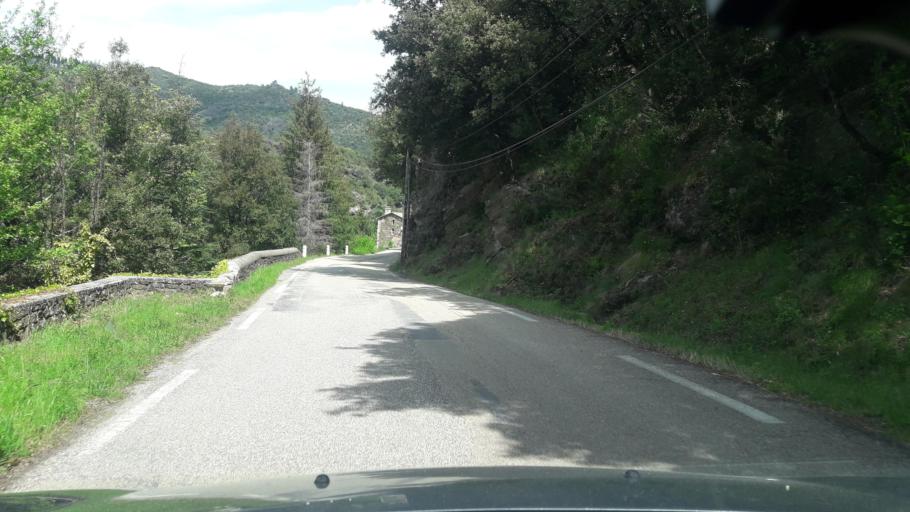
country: FR
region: Languedoc-Roussillon
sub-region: Departement du Gard
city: Valleraugue
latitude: 44.1189
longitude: 3.7289
